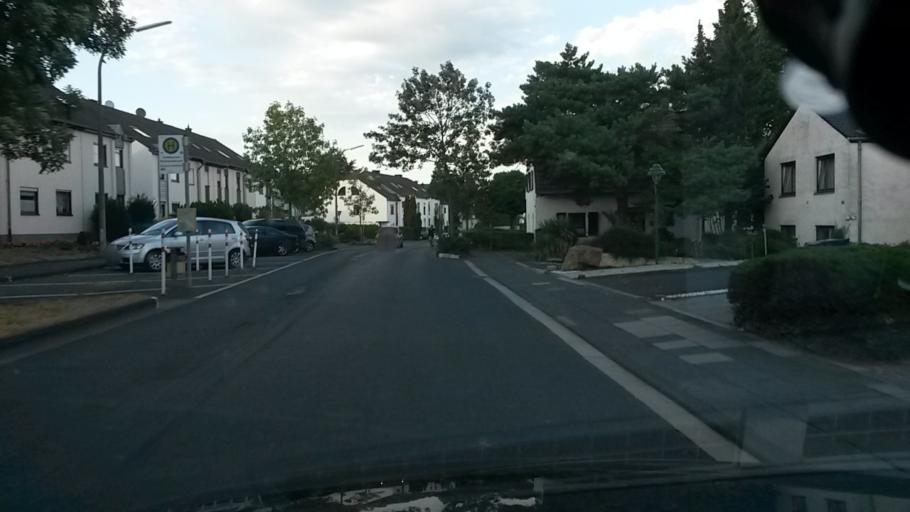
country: DE
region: North Rhine-Westphalia
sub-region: Regierungsbezirk Koln
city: Alfter
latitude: 50.7141
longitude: 7.0203
